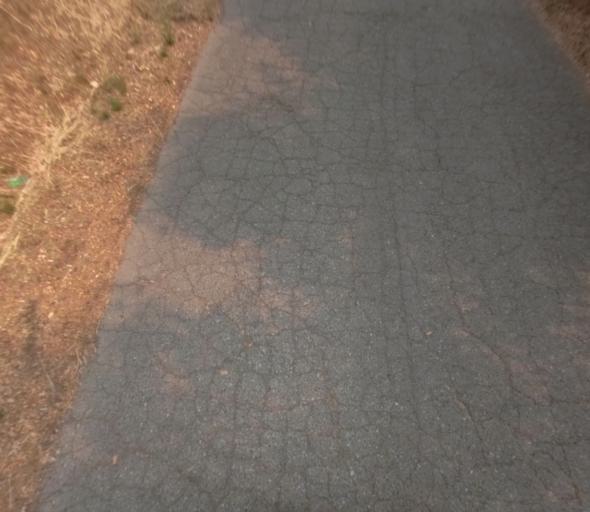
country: US
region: California
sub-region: Madera County
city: Oakhurst
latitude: 37.3011
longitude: -119.6041
